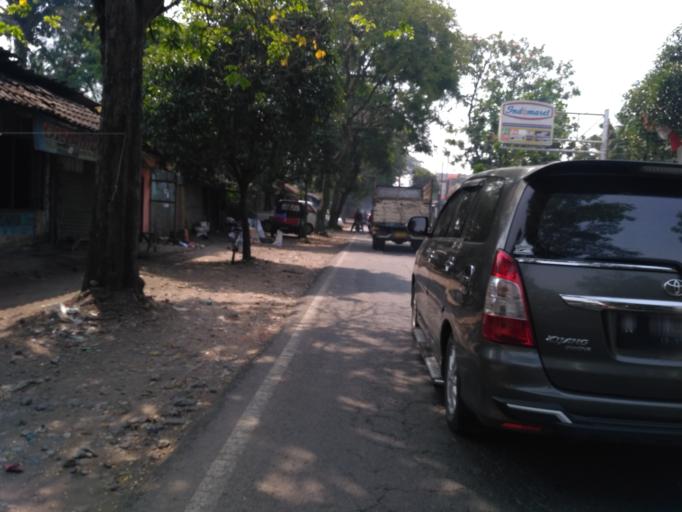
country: ID
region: East Java
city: Malang
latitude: -7.9858
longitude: 112.6560
